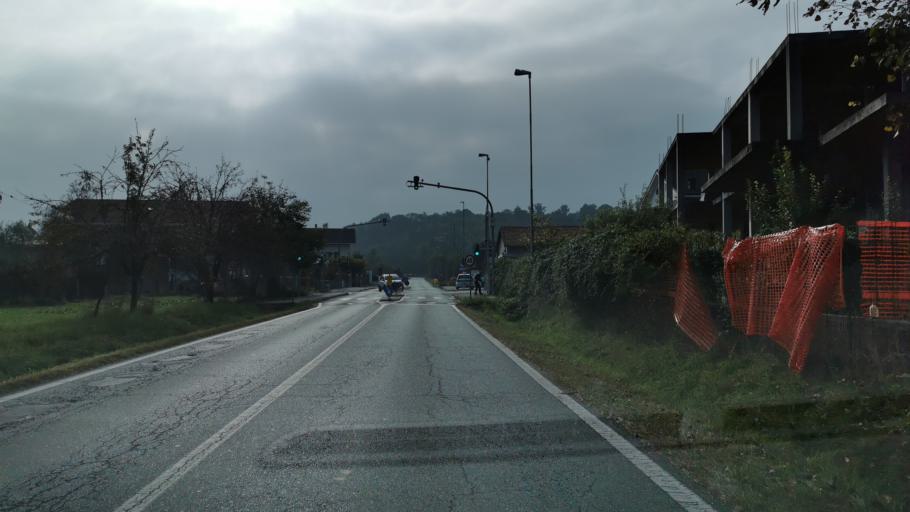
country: IT
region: Piedmont
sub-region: Provincia di Torino
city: Rivarossa
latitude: 45.2641
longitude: 7.6936
